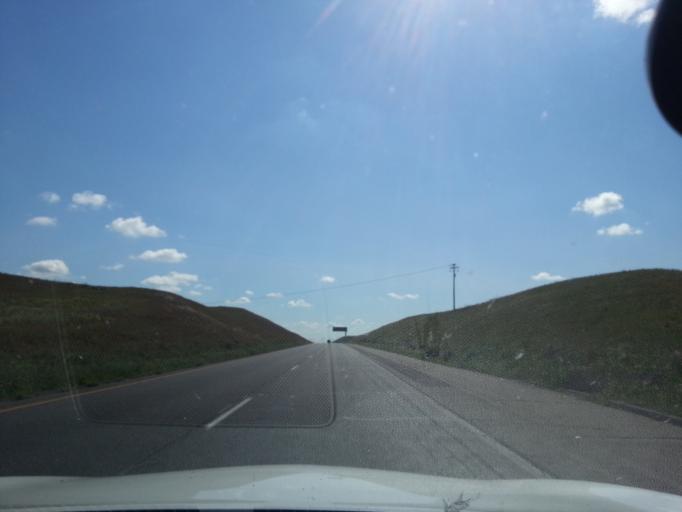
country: US
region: California
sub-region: Fresno County
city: Coalinga
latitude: 36.3119
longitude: -120.2846
